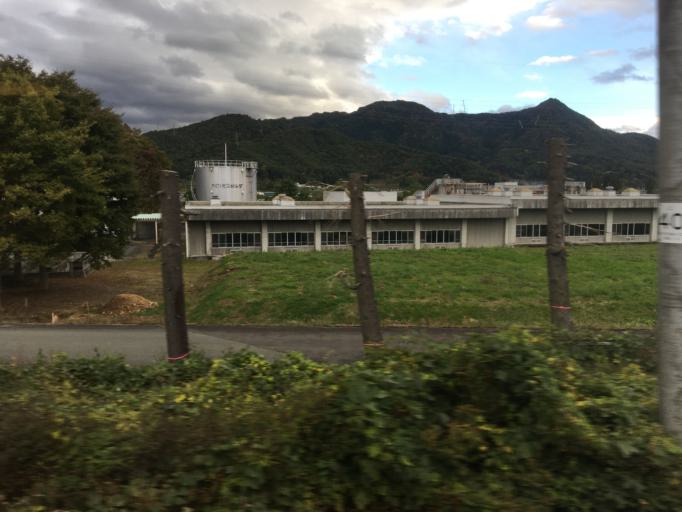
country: JP
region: Yamagata
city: Kaminoyama
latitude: 38.1666
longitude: 140.2917
